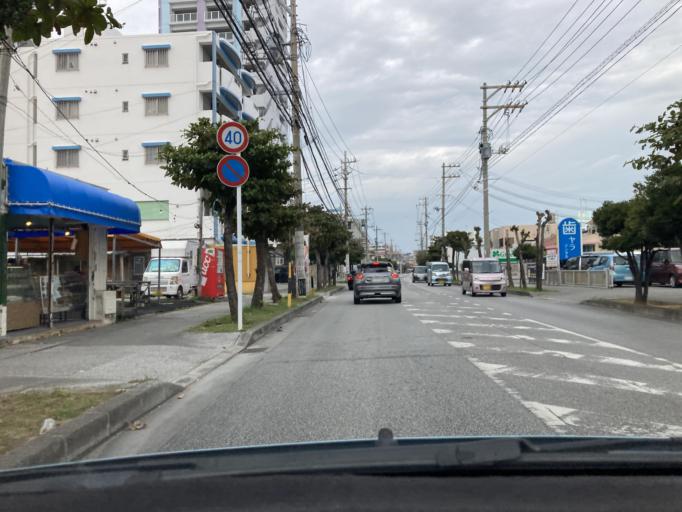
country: JP
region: Okinawa
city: Chatan
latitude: 26.3045
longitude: 127.7599
